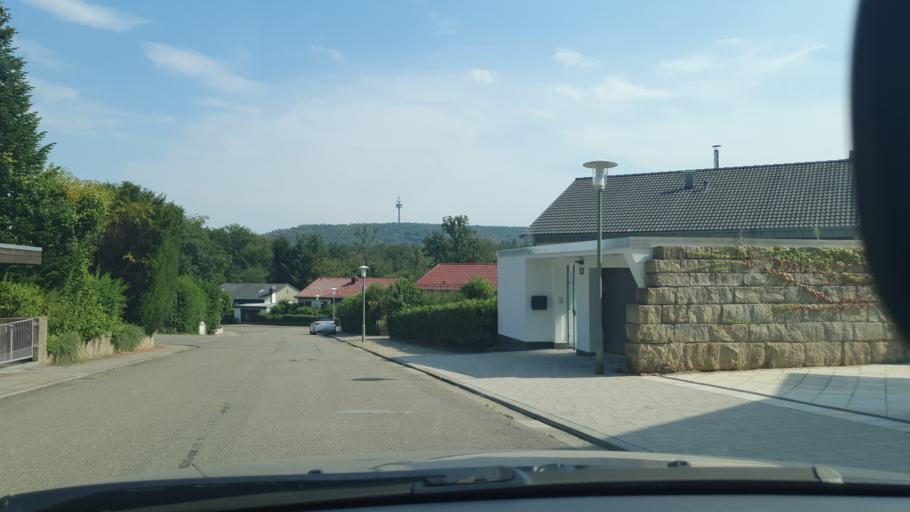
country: DE
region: Rheinland-Pfalz
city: Stelzenberg
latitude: 49.4286
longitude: 7.7235
